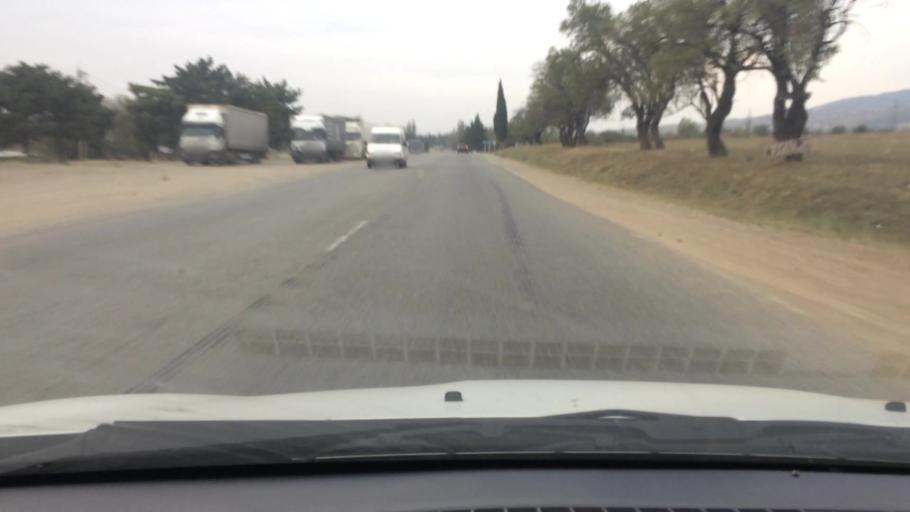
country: GE
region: T'bilisi
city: Tbilisi
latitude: 41.6339
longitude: 44.8185
